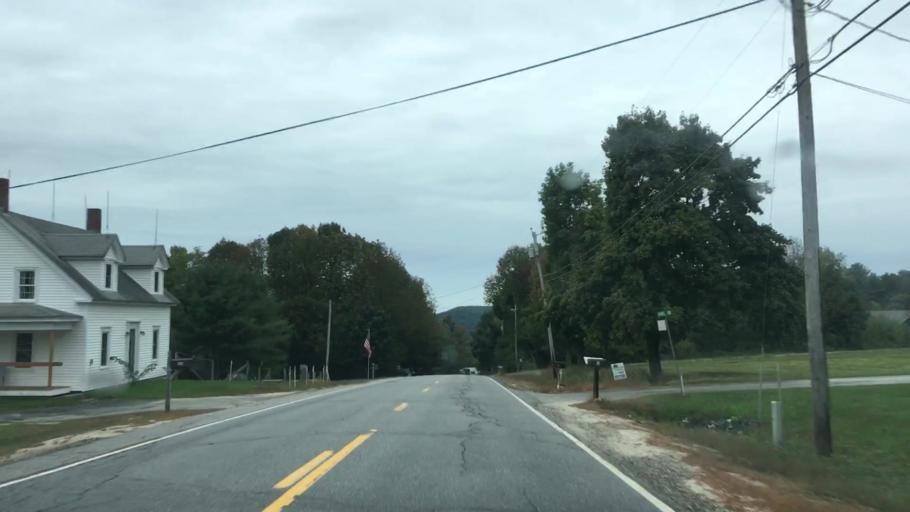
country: US
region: Maine
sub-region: Cumberland County
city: Raymond
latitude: 43.9395
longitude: -70.4506
